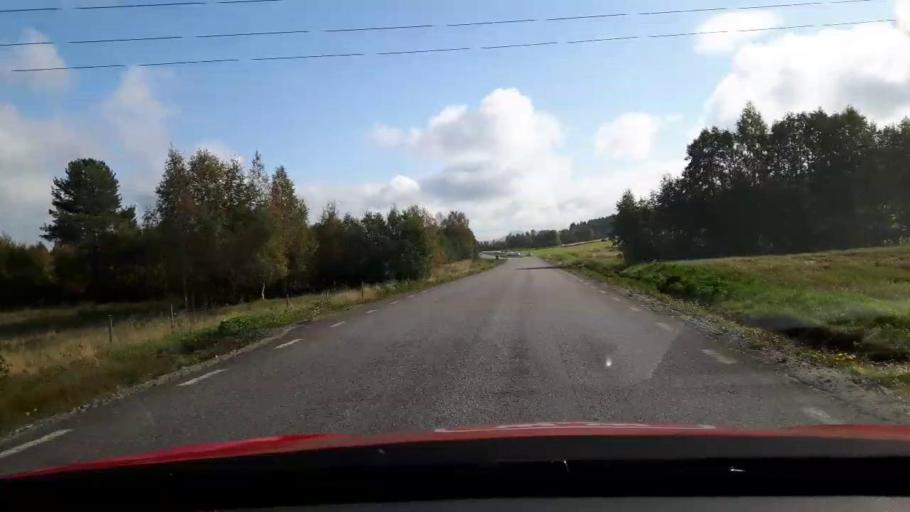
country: SE
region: Gaevleborg
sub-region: Ljusdals Kommun
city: Ljusdal
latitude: 61.7646
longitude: 16.0539
